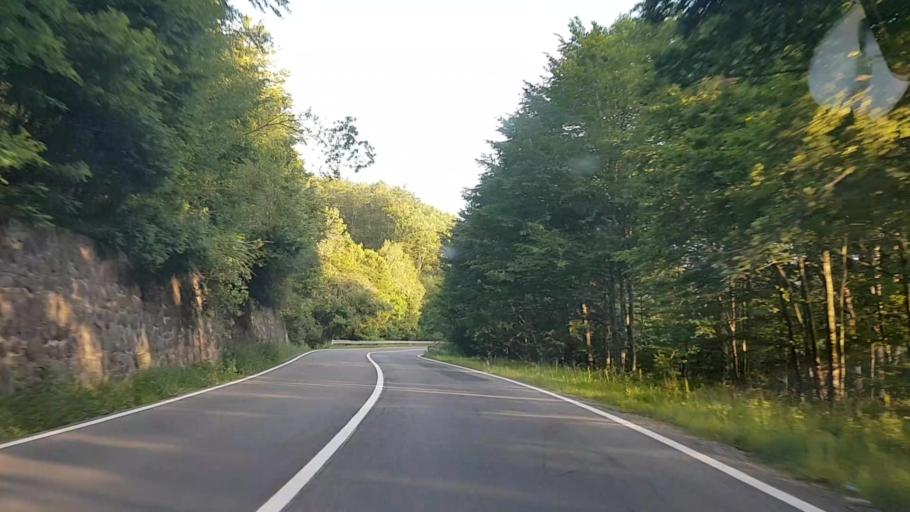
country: RO
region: Harghita
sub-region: Comuna Corund
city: Corund
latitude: 46.4456
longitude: 25.2283
